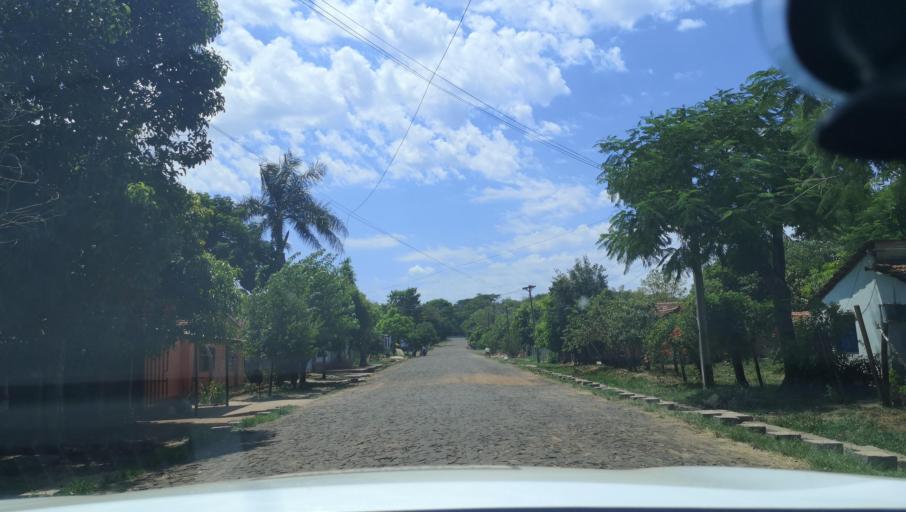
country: PY
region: Itapua
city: Carmen del Parana
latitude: -27.1642
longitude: -56.2339
